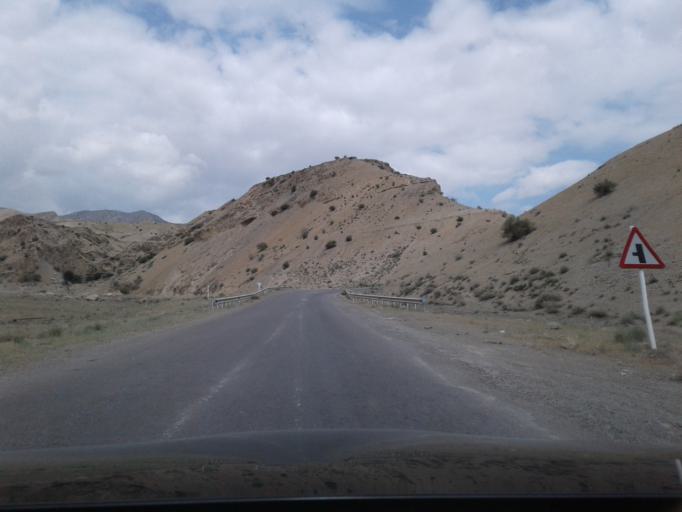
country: TM
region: Ahal
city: Baharly
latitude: 38.5028
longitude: 57.0821
